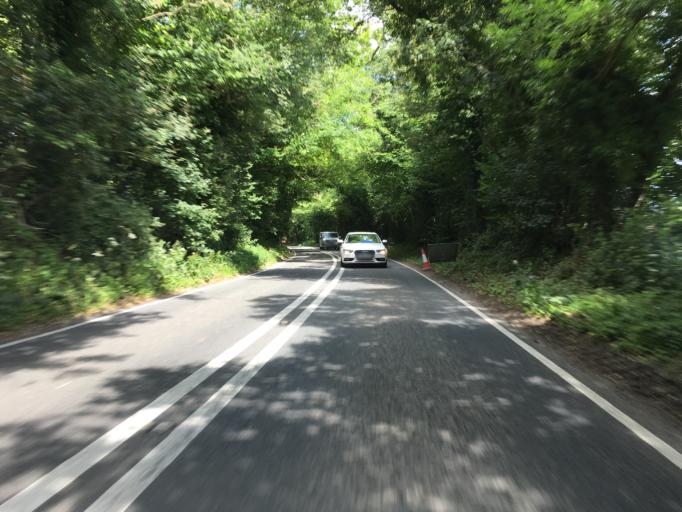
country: GB
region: England
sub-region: Hampshire
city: Highclere
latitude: 51.3161
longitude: -1.3832
